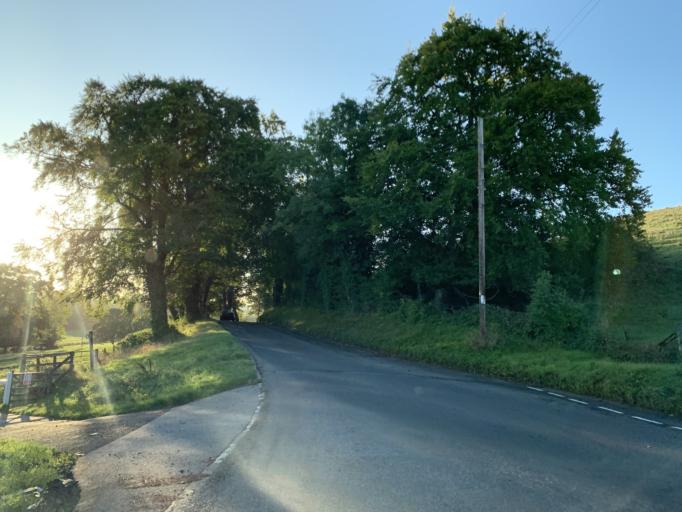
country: GB
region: England
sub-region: Wiltshire
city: Woodford
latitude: 51.1052
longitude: -1.8303
